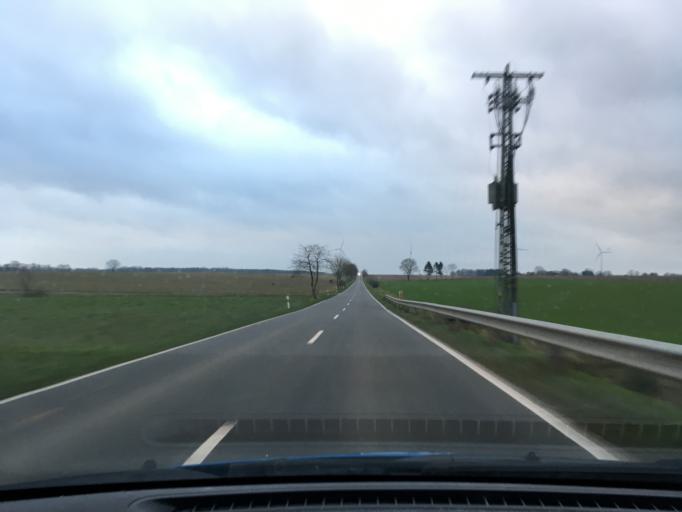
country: DE
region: Lower Saxony
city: Hermannsburg
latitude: 52.8453
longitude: 10.0691
